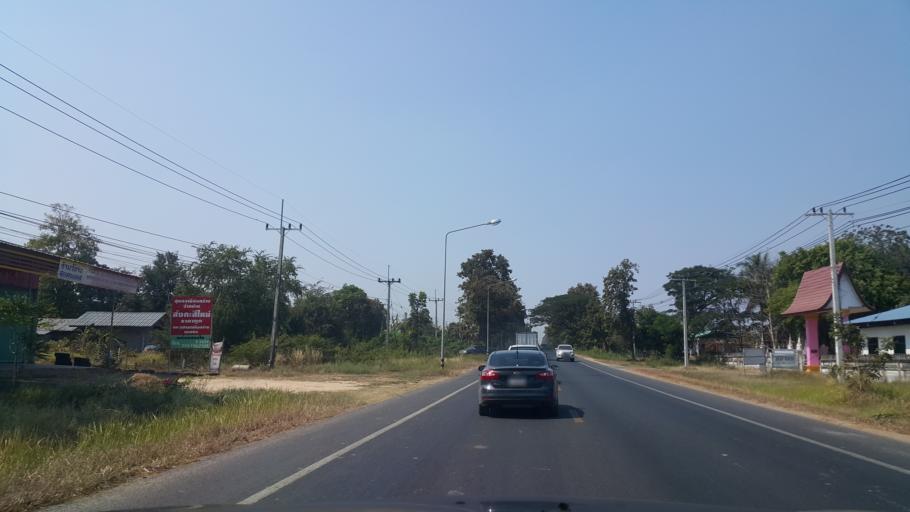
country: TH
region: Nakhon Ratchasima
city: Lam Thamen Chai
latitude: 15.3596
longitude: 102.8654
